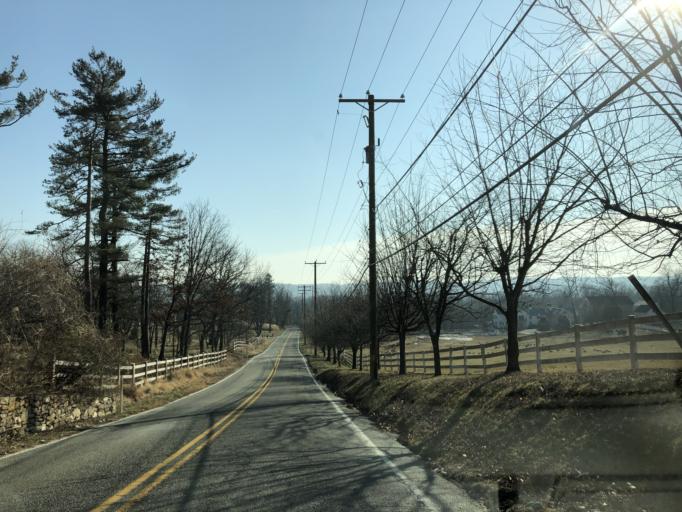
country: US
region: Pennsylvania
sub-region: Chester County
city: Chesterbrook
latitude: 40.0797
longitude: -75.4857
